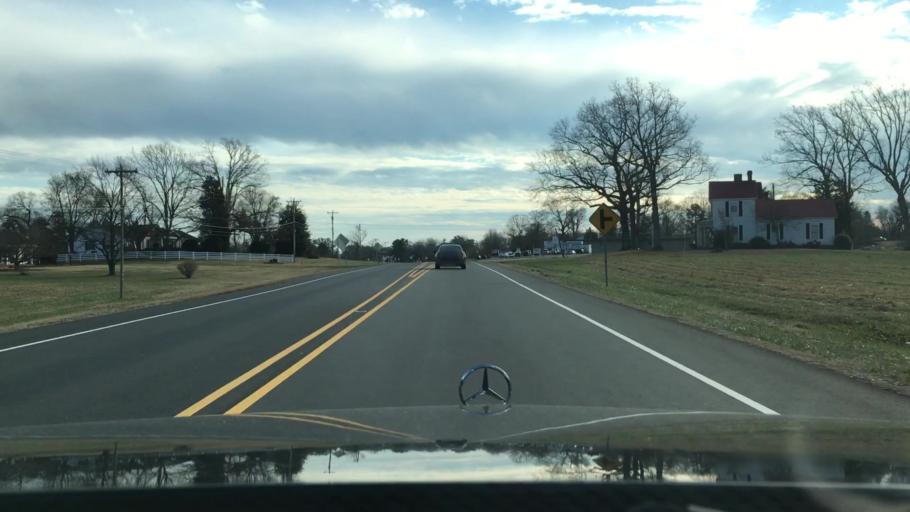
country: US
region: Virginia
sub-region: City of Danville
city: Danville
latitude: 36.5363
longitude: -79.4002
